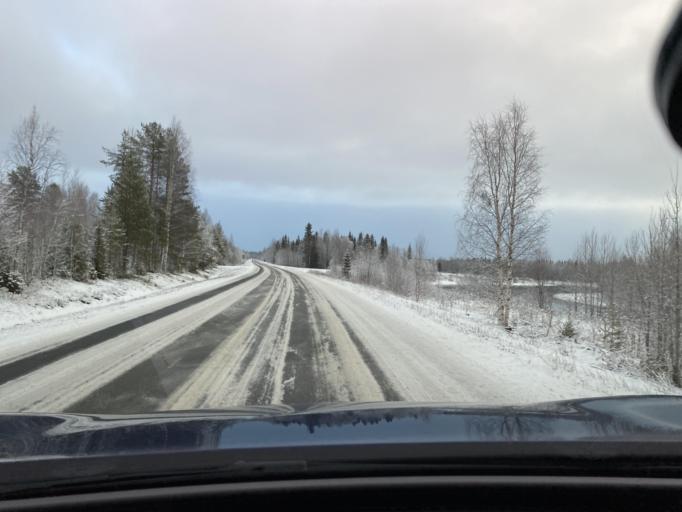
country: FI
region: Lapland
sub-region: Rovaniemi
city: Ranua
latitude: 65.9621
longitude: 26.0333
